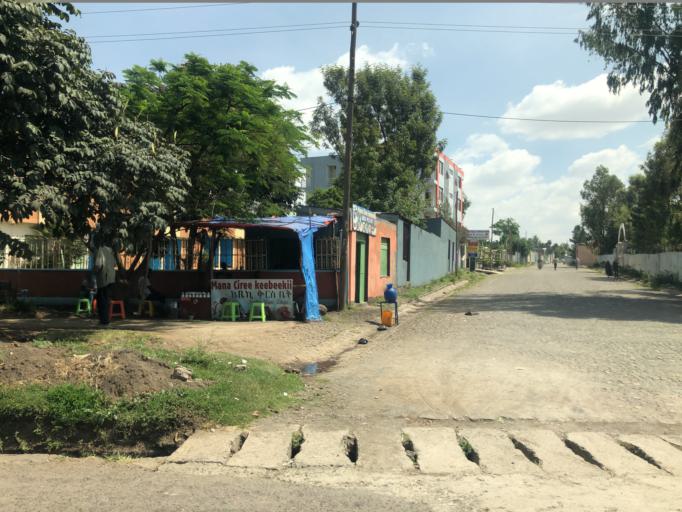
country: ET
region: Oromiya
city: Shashemene
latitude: 7.2001
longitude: 38.6063
